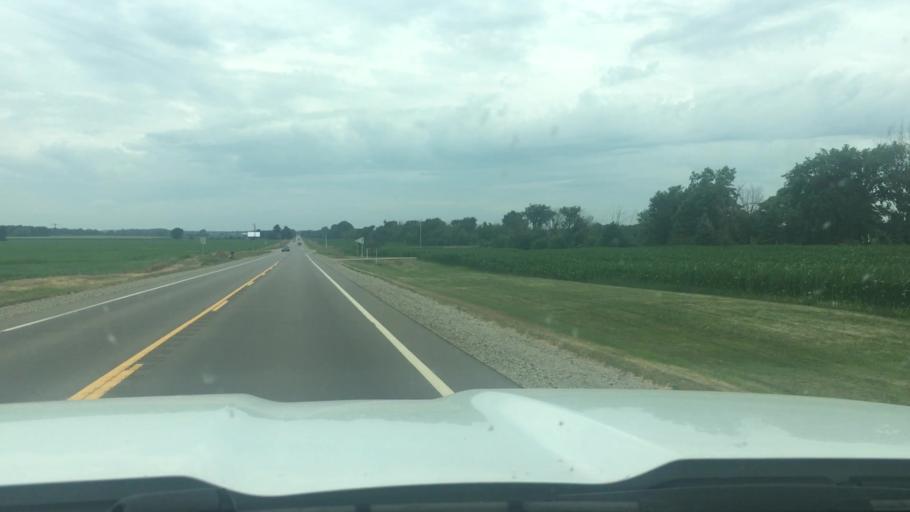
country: US
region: Michigan
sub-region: Clinton County
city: Fowler
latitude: 43.0019
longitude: -84.7750
